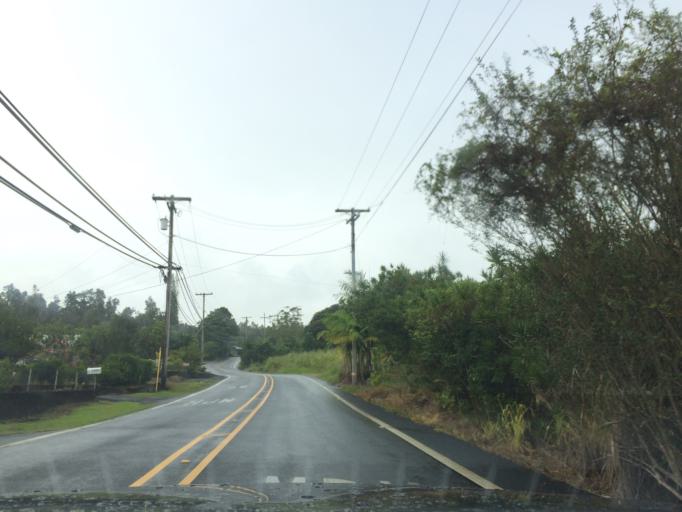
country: US
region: Hawaii
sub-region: Hawaii County
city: Hilo
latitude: 19.6898
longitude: -155.1266
